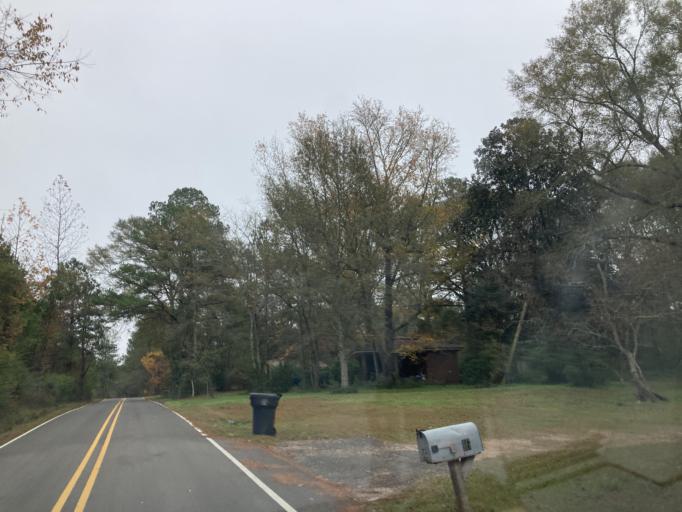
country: US
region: Mississippi
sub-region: Lamar County
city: Lumberton
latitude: 31.0650
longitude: -89.4211
